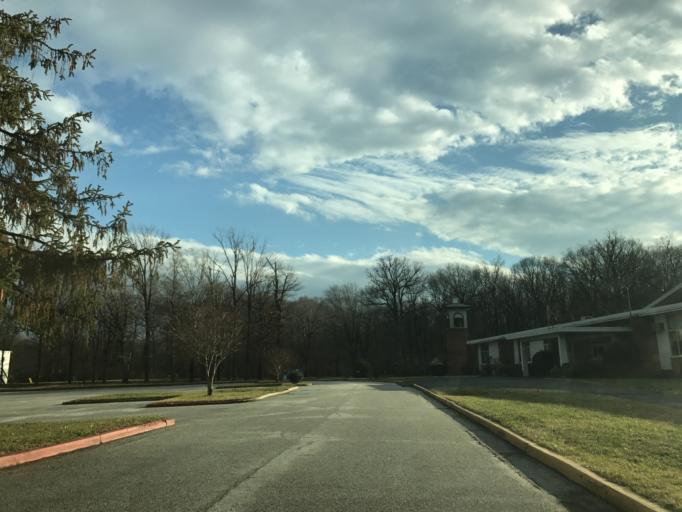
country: US
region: Maryland
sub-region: Baltimore County
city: Edgemere
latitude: 39.2353
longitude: -76.4437
